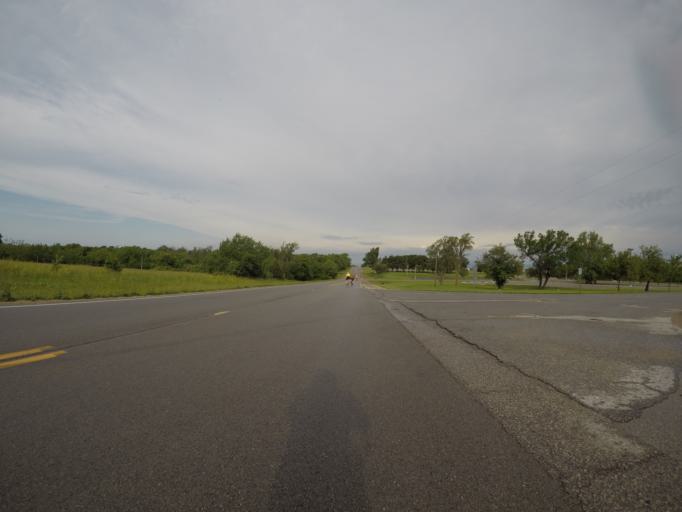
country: US
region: Kansas
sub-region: Shawnee County
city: Auburn
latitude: 38.9566
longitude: -95.7512
